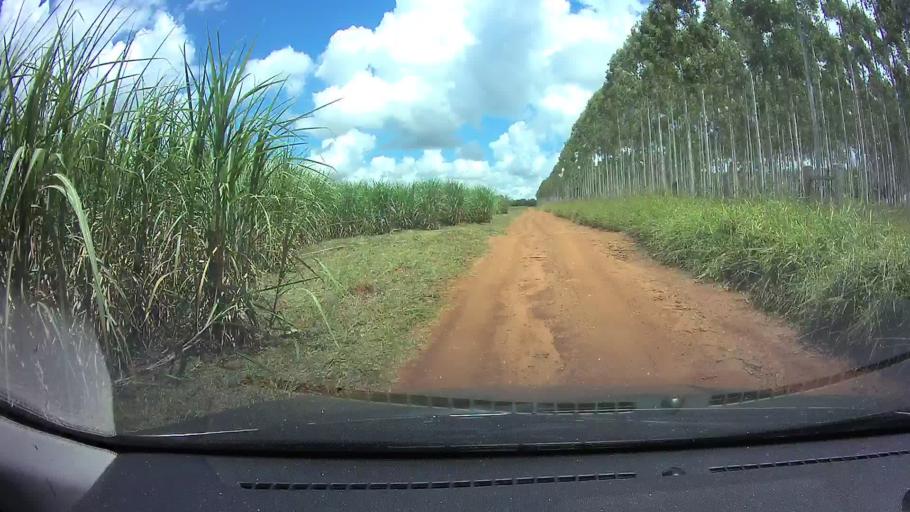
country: PY
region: Paraguari
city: La Colmena
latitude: -25.9622
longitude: -56.7316
